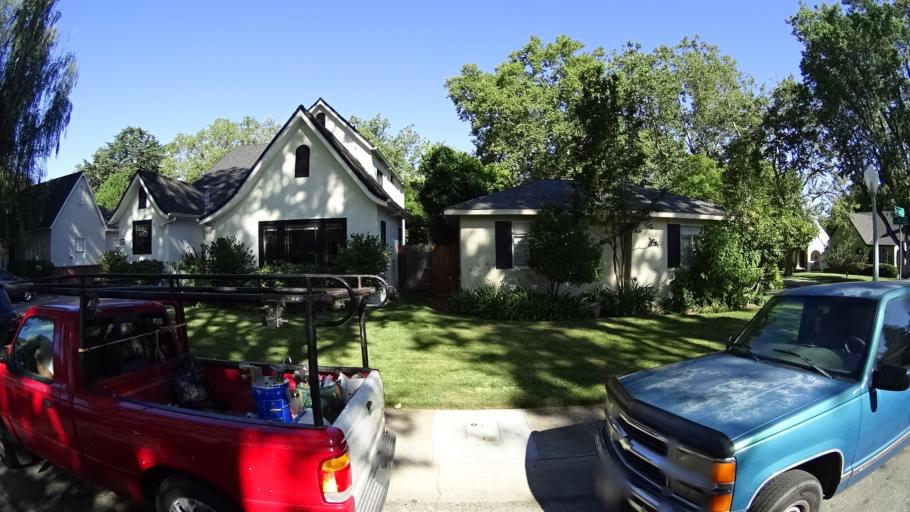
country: US
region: California
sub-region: Sacramento County
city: Sacramento
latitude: 38.5697
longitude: -121.4470
